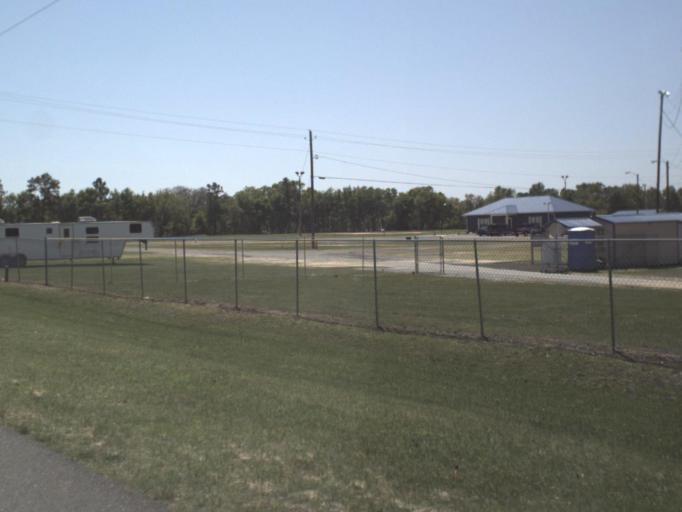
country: US
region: Florida
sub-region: Escambia County
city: Ensley
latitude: 30.5036
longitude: -87.3059
